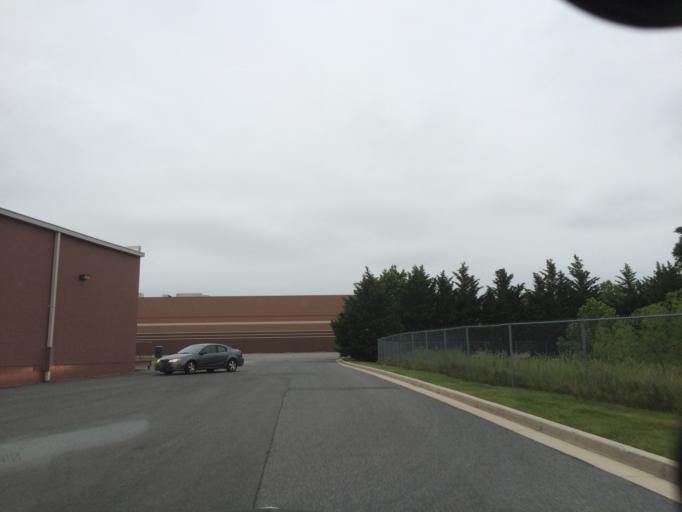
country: US
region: Maryland
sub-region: Washington County
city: Halfway
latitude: 39.6204
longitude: -77.7750
